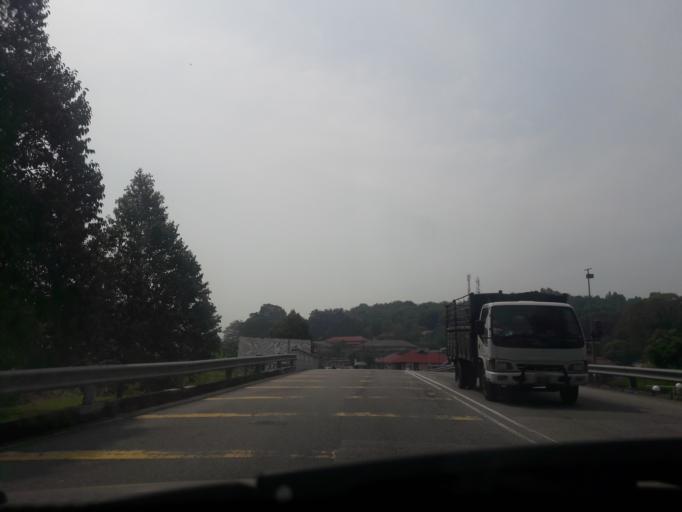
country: MY
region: Kedah
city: Kulim
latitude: 5.3689
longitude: 100.5569
